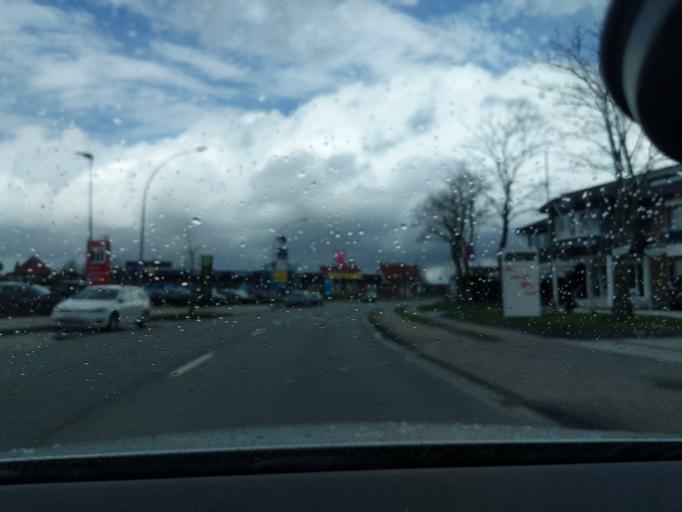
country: DE
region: Lower Saxony
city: Stade
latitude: 53.6084
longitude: 9.4766
